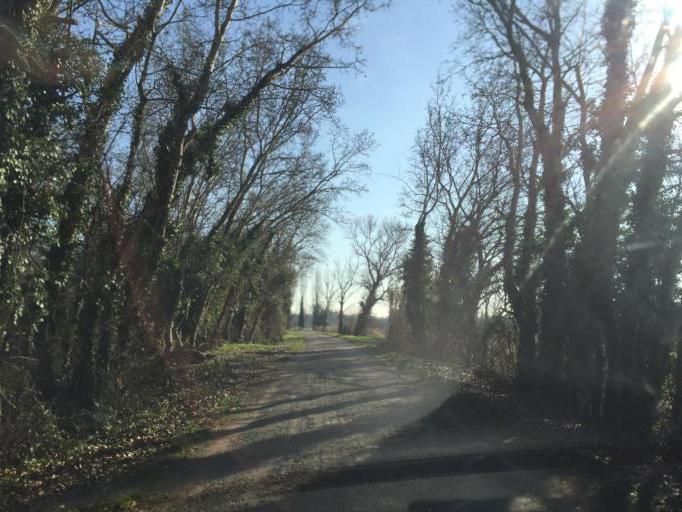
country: FR
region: Provence-Alpes-Cote d'Azur
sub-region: Departement du Vaucluse
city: Courthezon
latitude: 44.0789
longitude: 4.9247
